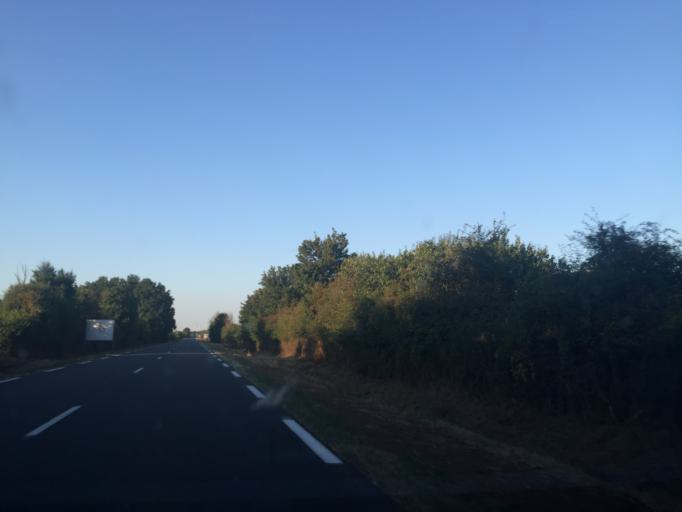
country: FR
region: Poitou-Charentes
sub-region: Departement de la Vienne
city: Saint-Sauvant
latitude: 46.3747
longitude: 0.0345
